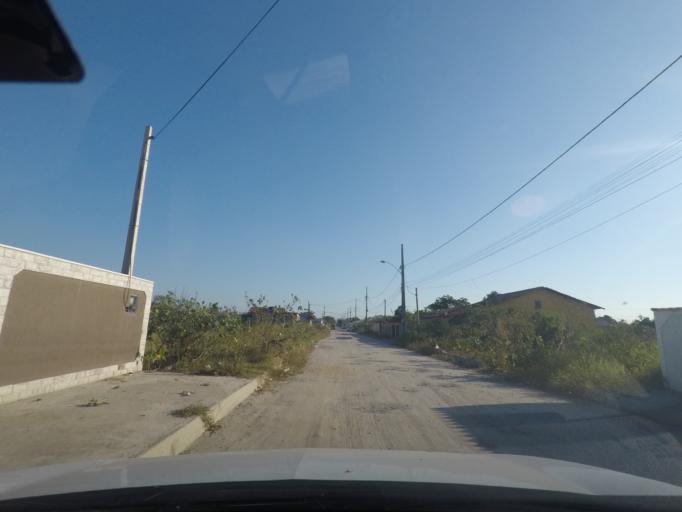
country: BR
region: Rio de Janeiro
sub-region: Marica
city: Marica
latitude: -22.9631
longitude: -42.9360
